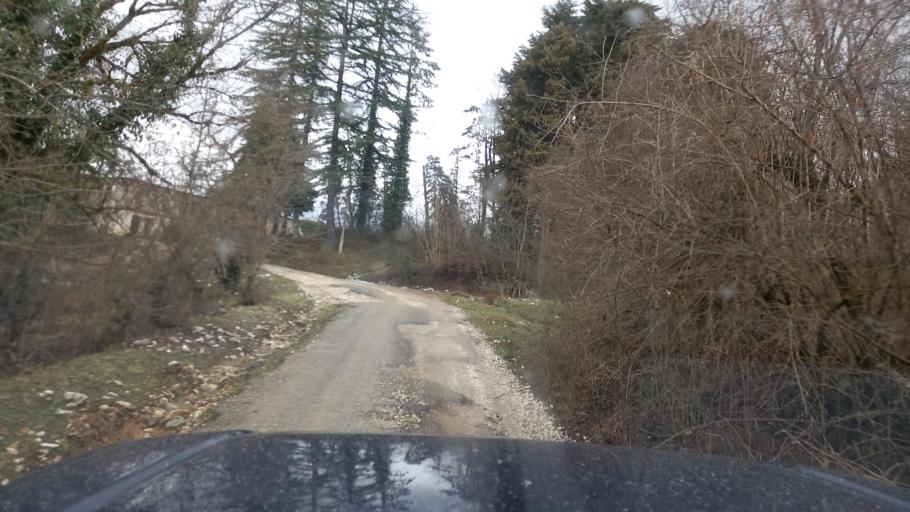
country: GE
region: Abkhazia
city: Dranda
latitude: 43.0359
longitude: 41.3228
